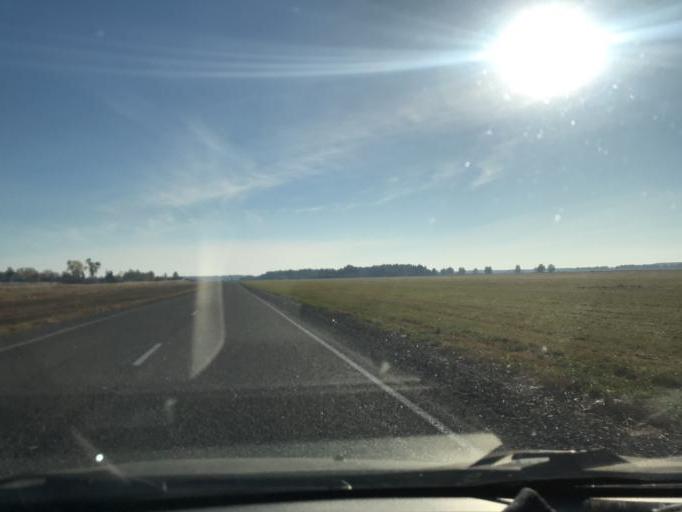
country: BY
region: Gomel
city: Brahin
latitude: 51.7753
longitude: 30.2565
